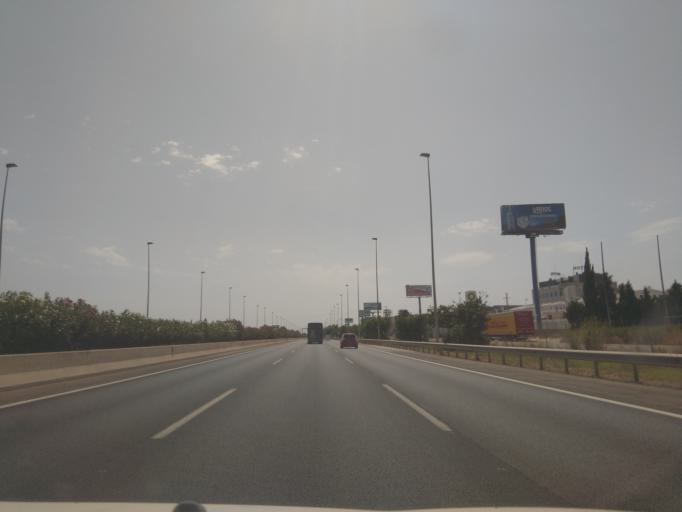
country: ES
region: Valencia
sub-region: Provincia de Valencia
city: Catarroja
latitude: 39.3980
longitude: -0.3887
